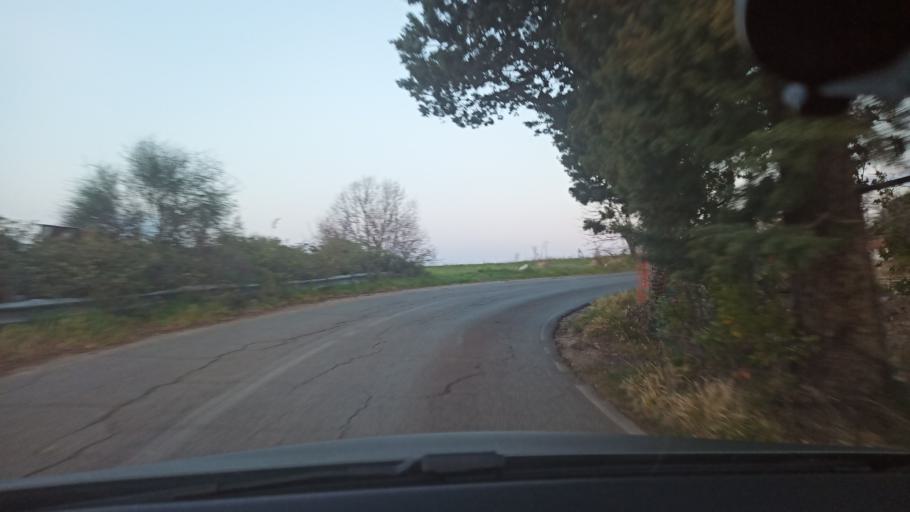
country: IT
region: Latium
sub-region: Provincia di Rieti
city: Montasola
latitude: 42.3640
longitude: 12.6723
